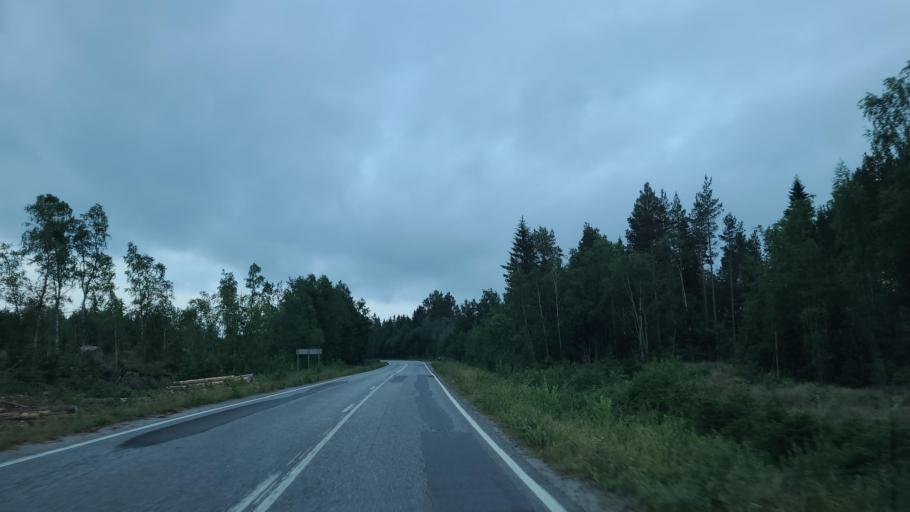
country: FI
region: Ostrobothnia
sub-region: Vaasa
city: Replot
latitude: 63.2766
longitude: 21.1368
